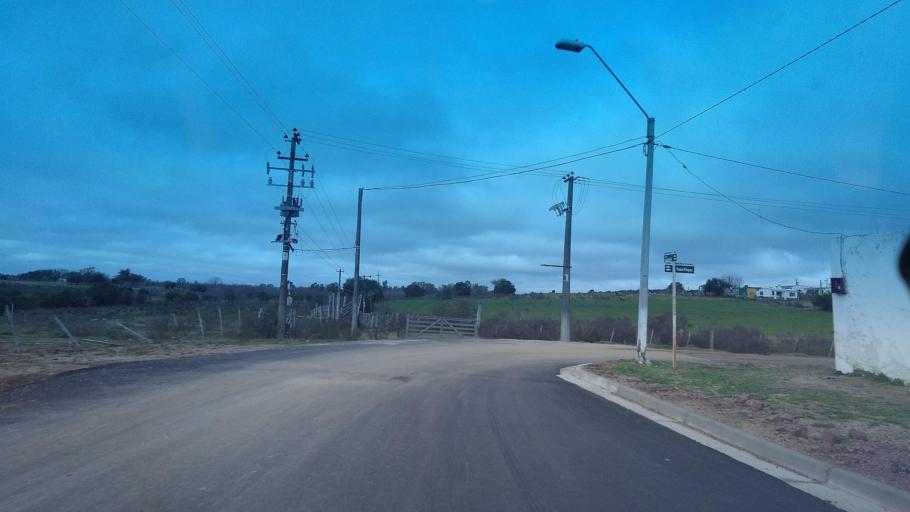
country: UY
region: Canelones
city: Tala
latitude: -34.2049
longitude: -55.7400
